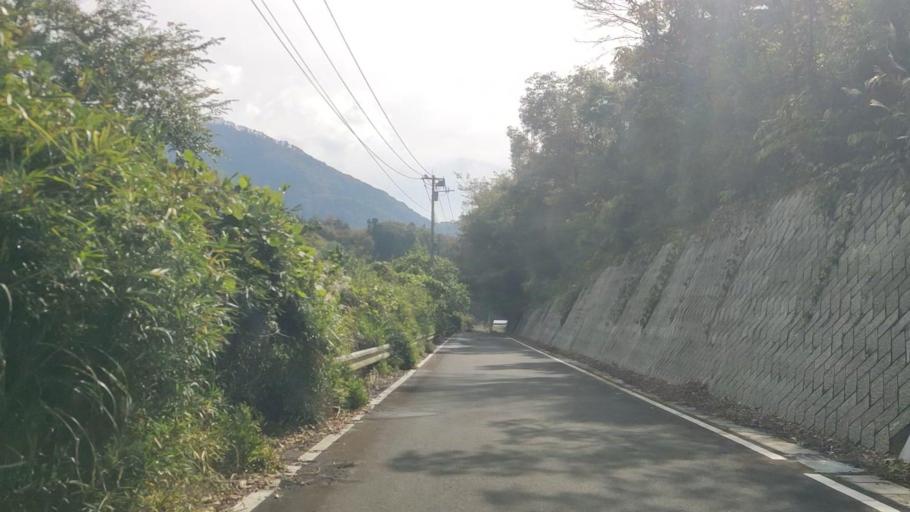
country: JP
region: Yamanashi
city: Ryuo
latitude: 35.4507
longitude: 138.4487
